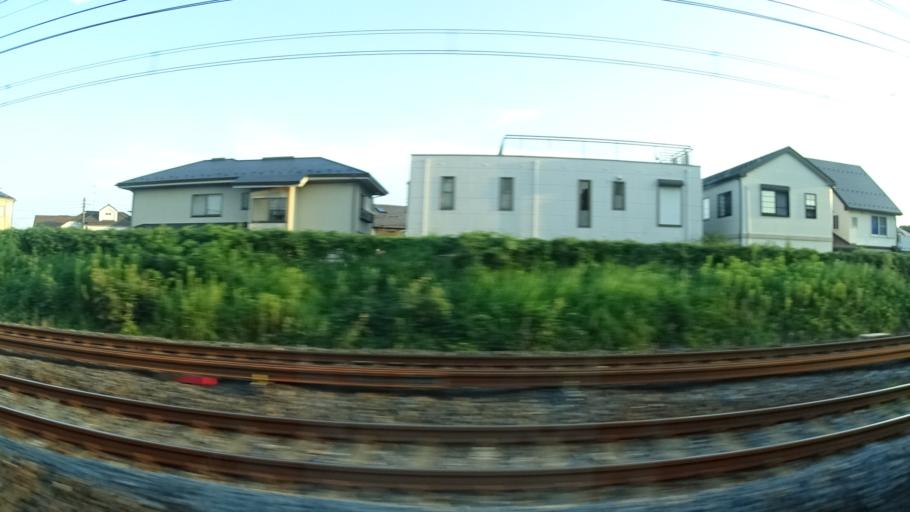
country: JP
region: Chiba
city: Abiko
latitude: 35.8735
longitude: 139.9977
